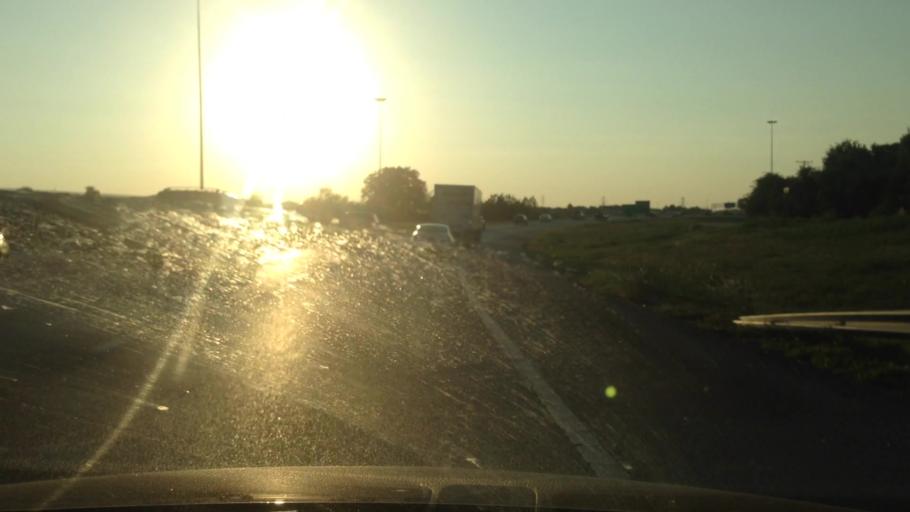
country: US
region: Texas
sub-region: Tarrant County
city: Kennedale
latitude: 32.6695
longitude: -97.2353
